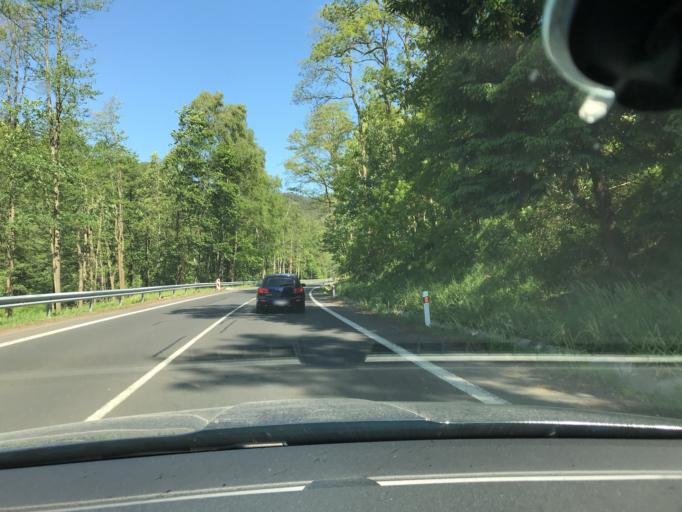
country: CZ
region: Karlovarsky
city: Jachymov
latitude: 50.3406
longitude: 12.9379
